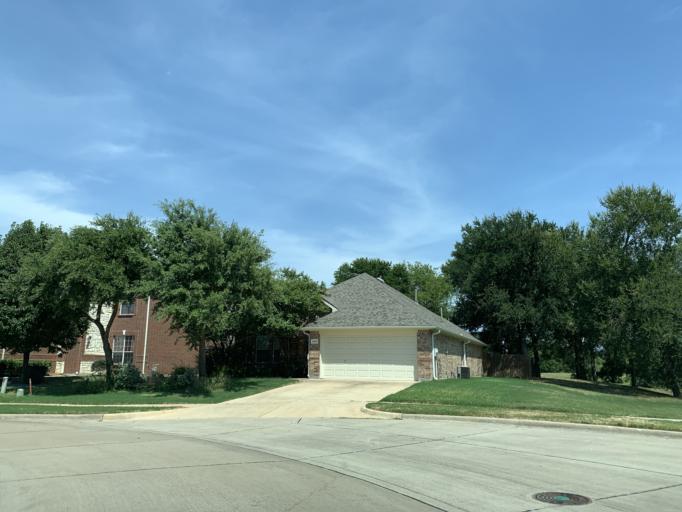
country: US
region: Texas
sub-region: Dallas County
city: Cedar Hill
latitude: 32.6436
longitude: -97.0197
